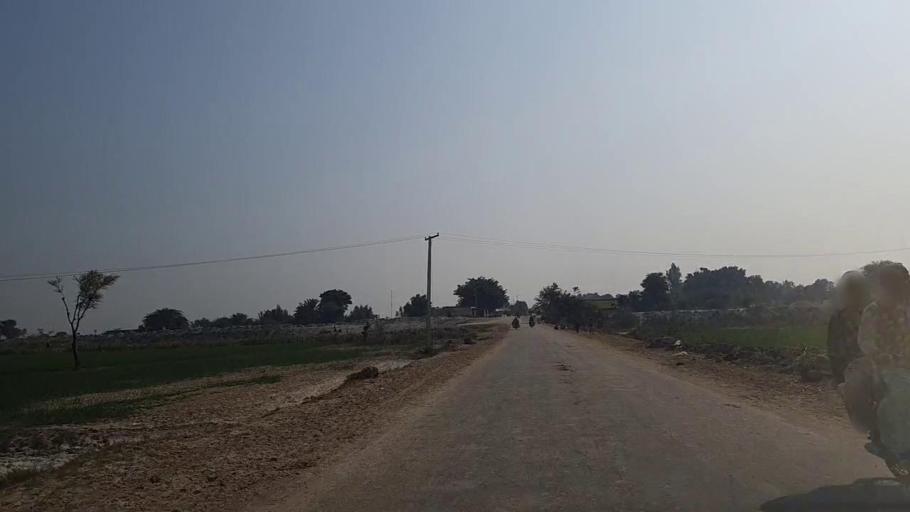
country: PK
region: Sindh
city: Jam Sahib
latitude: 26.3342
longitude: 68.5364
